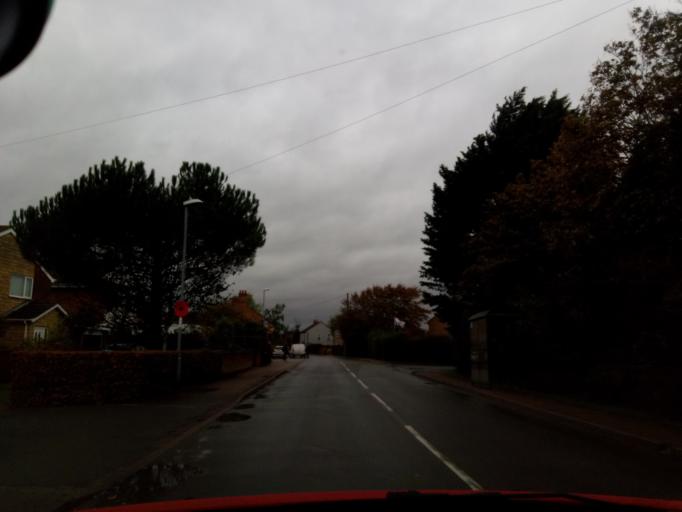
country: GB
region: England
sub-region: Cambridgeshire
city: Sawtry
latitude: 52.4326
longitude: -0.2781
